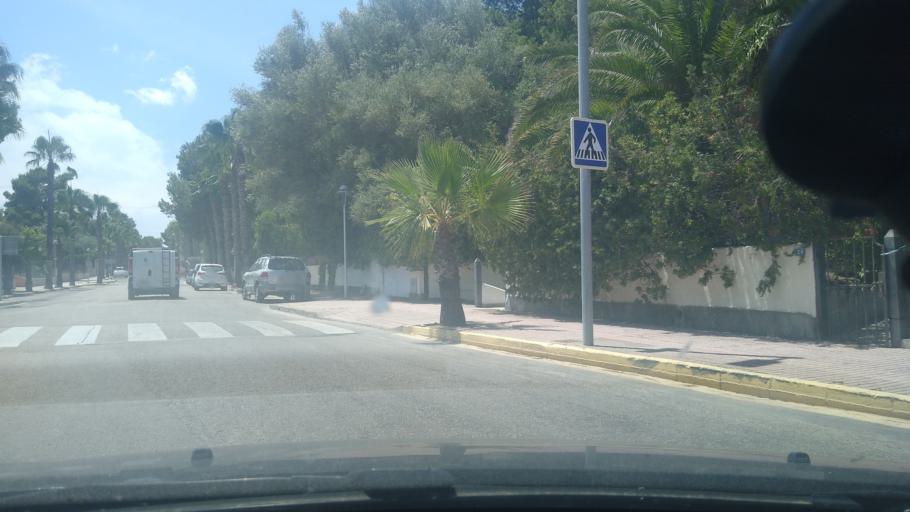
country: ES
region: Balearic Islands
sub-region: Illes Balears
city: Santa Margalida
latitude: 39.7595
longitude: 3.1595
